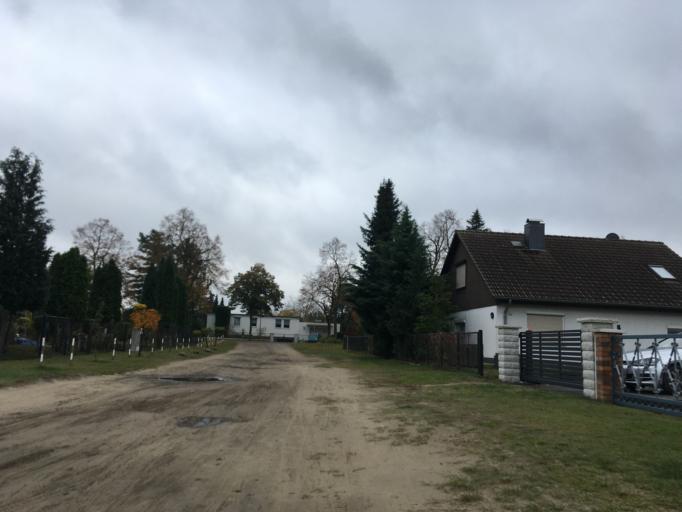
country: DE
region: Brandenburg
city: Furstenwalde
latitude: 52.3530
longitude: 14.0514
